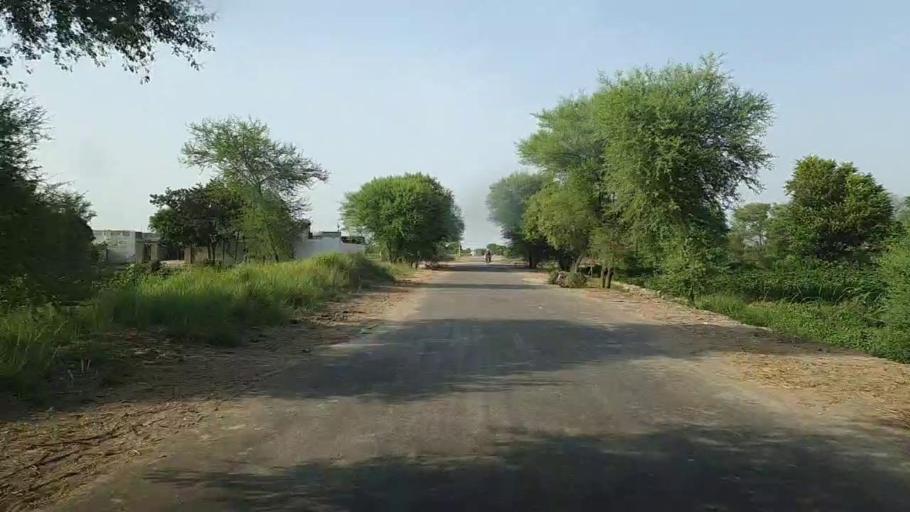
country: PK
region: Sindh
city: Ubauro
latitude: 28.0914
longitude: 69.8445
